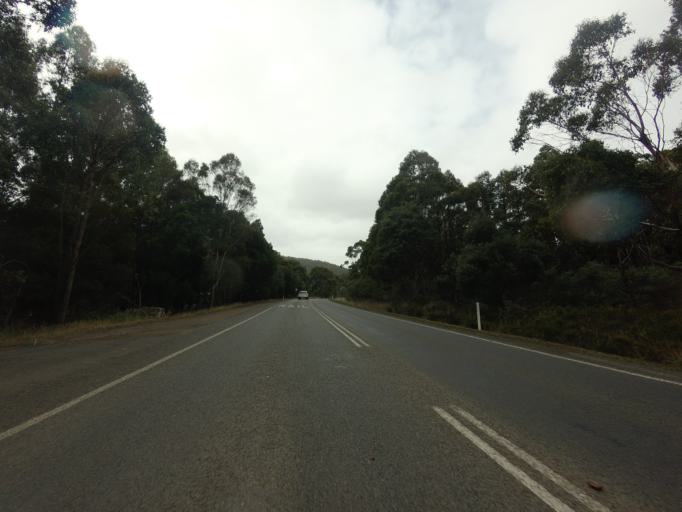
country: AU
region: Tasmania
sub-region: Derwent Valley
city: New Norfolk
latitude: -42.6824
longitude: 146.7362
